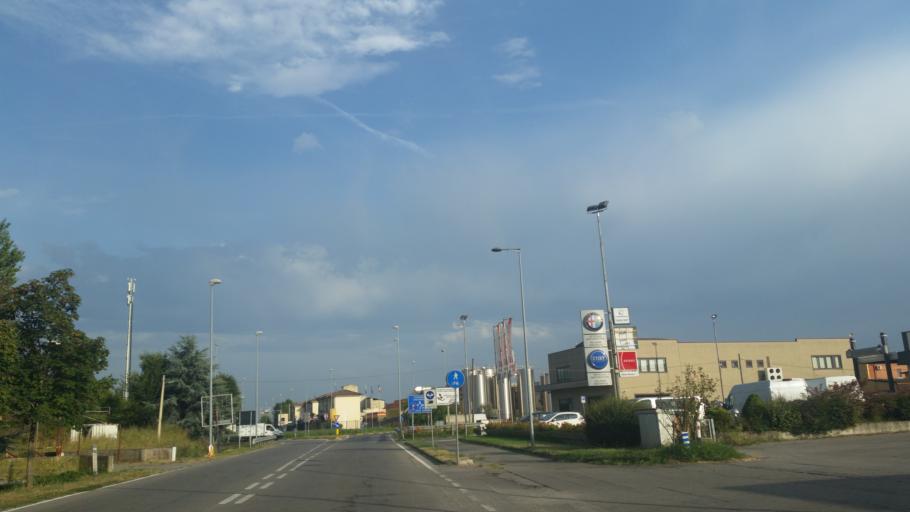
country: IT
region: Lombardy
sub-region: Provincia di Brescia
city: San Paolo
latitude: 45.3634
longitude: 10.0438
